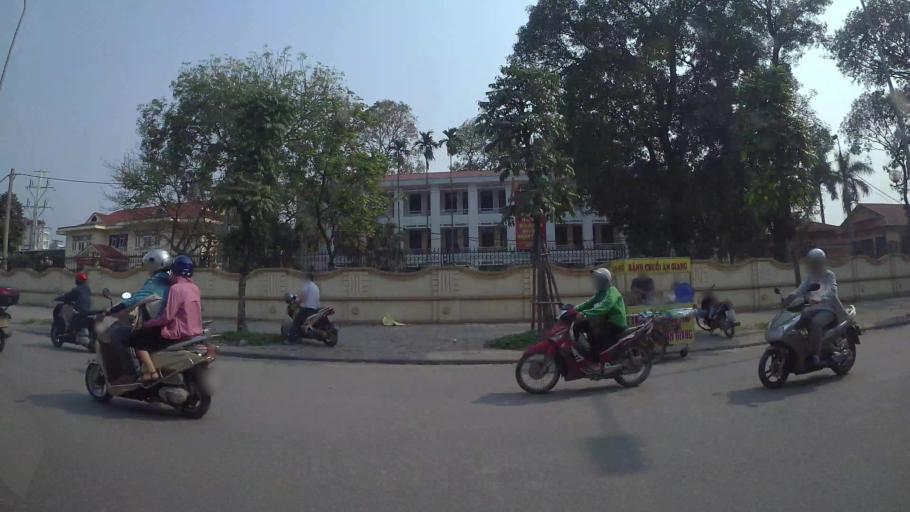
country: VN
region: Ha Noi
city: Hai BaTrung
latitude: 20.9990
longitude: 105.8352
